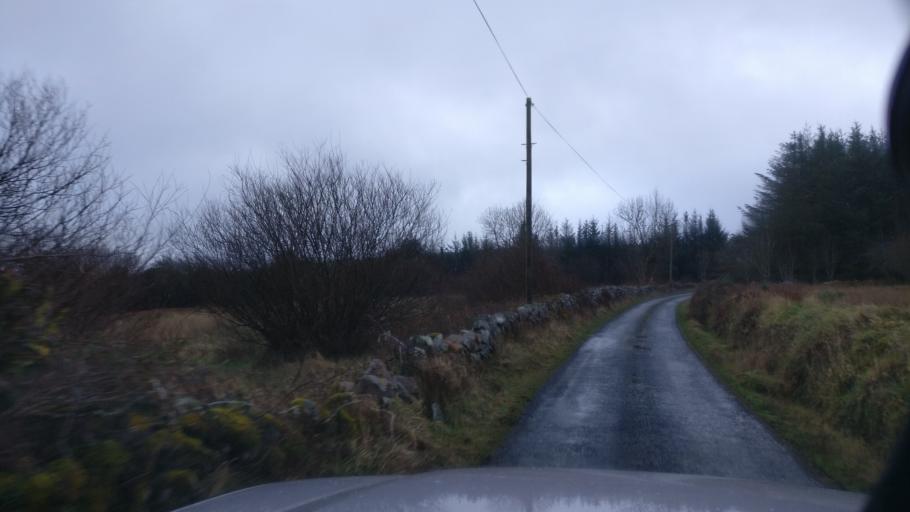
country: IE
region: Connaught
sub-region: County Galway
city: Loughrea
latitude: 53.1500
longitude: -8.6172
